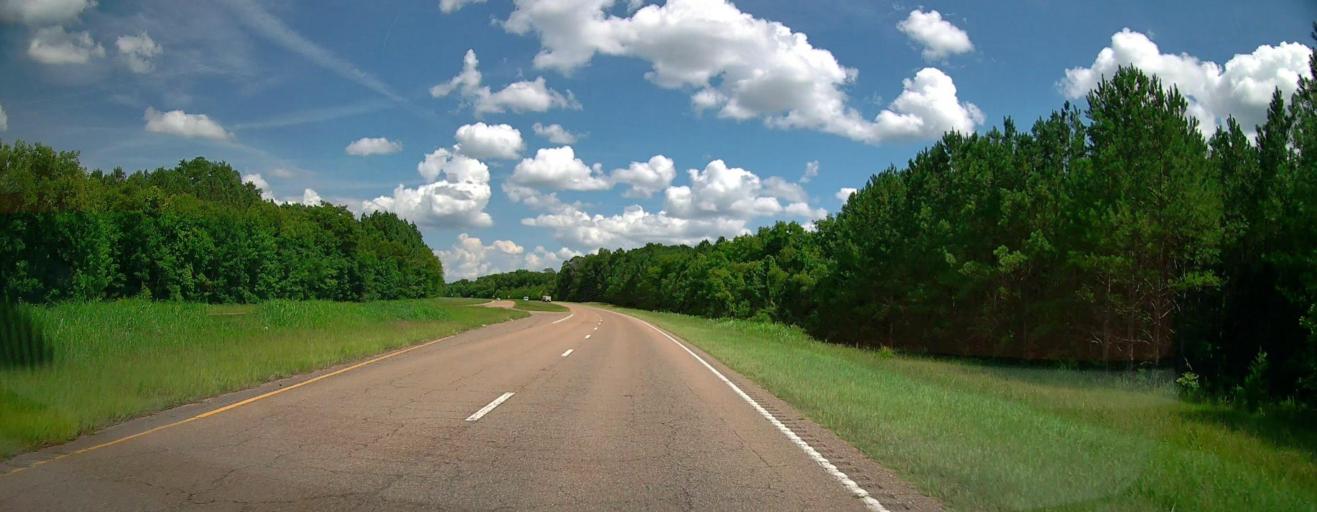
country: US
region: Mississippi
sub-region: Monroe County
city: Aberdeen
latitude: 33.8177
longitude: -88.5794
